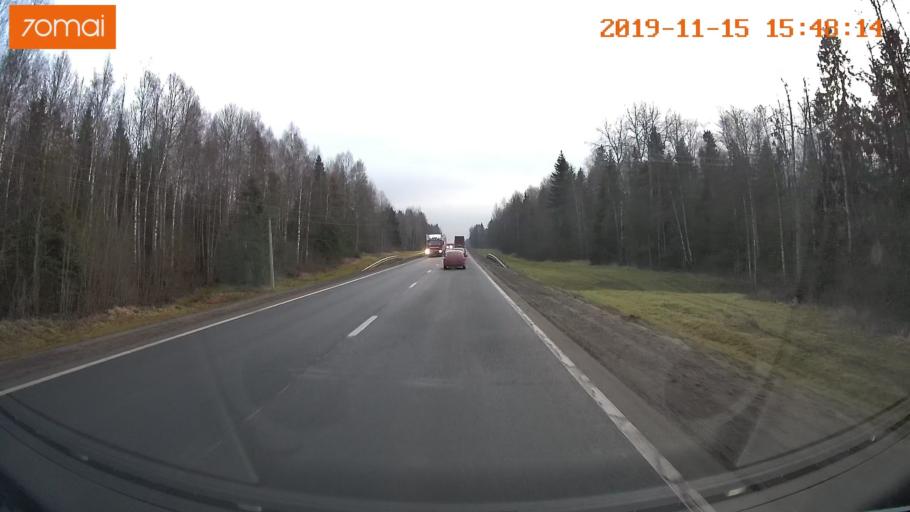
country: RU
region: Jaroslavl
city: Danilov
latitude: 57.9295
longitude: 40.0065
